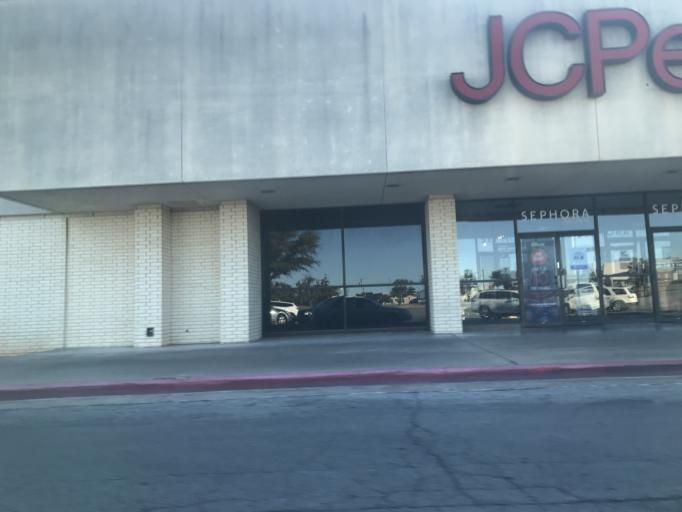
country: US
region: Texas
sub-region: Tom Green County
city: San Angelo
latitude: 31.4286
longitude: -100.5005
